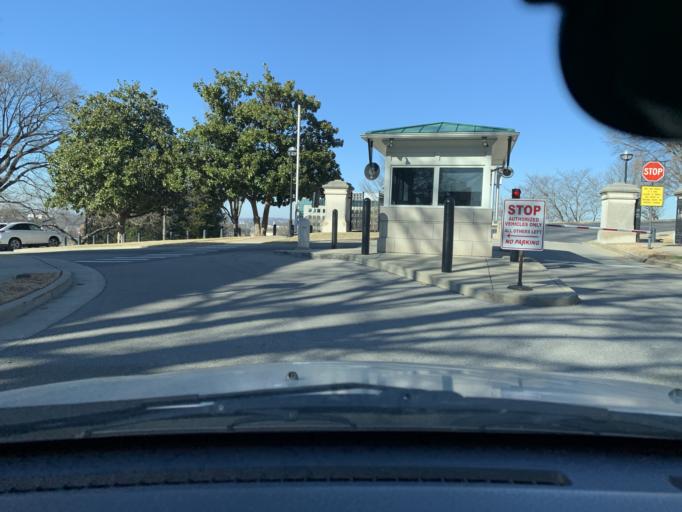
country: US
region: Tennessee
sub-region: Davidson County
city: Nashville
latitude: 36.1658
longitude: -86.7851
